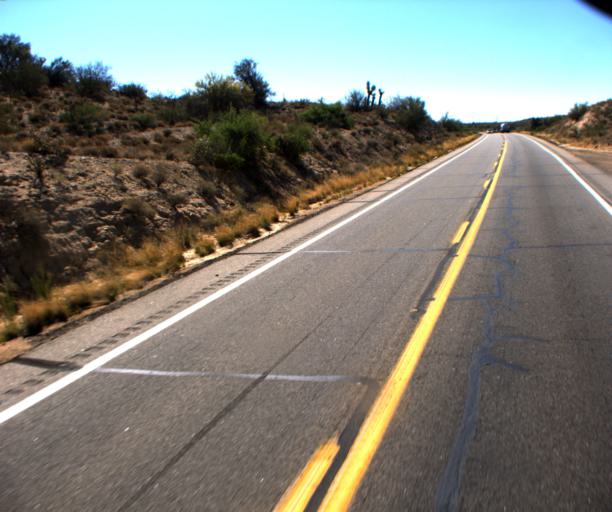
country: US
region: Arizona
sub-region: Yavapai County
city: Bagdad
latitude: 34.3489
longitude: -113.1628
